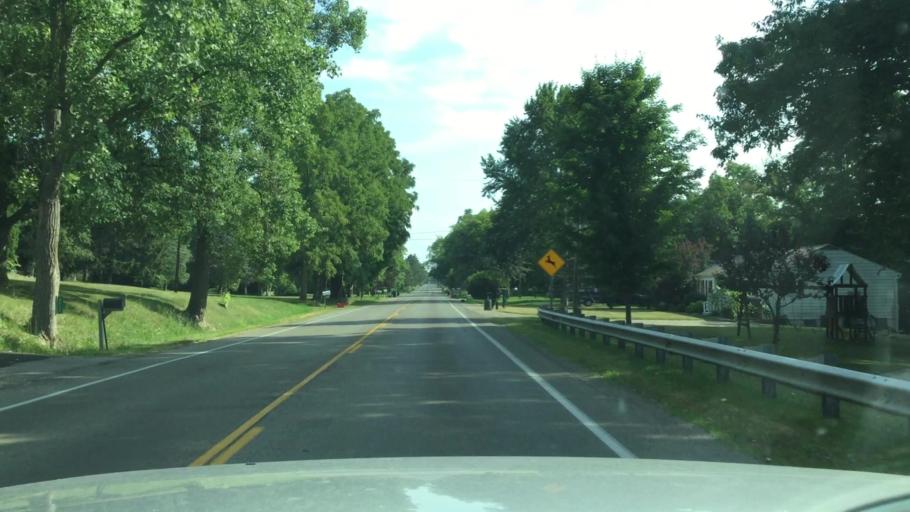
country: US
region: Michigan
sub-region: Genesee County
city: Flushing
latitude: 43.0746
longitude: -83.8726
